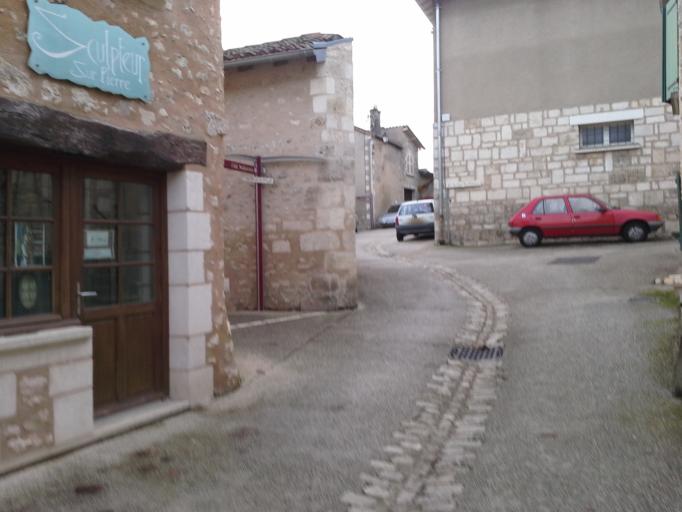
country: FR
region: Poitou-Charentes
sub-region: Departement de la Vienne
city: Chauvigny
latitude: 46.5715
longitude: 0.6487
